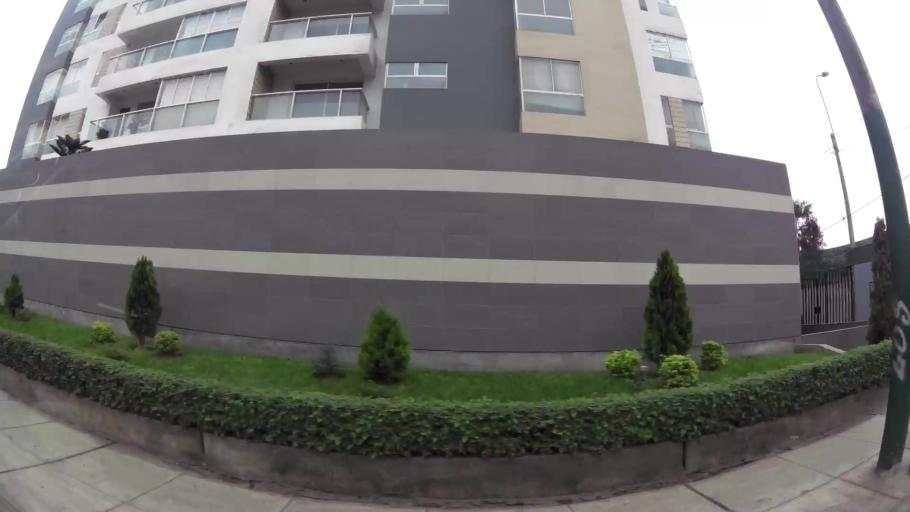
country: PE
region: Lima
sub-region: Lima
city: La Molina
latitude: -12.0929
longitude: -76.9674
